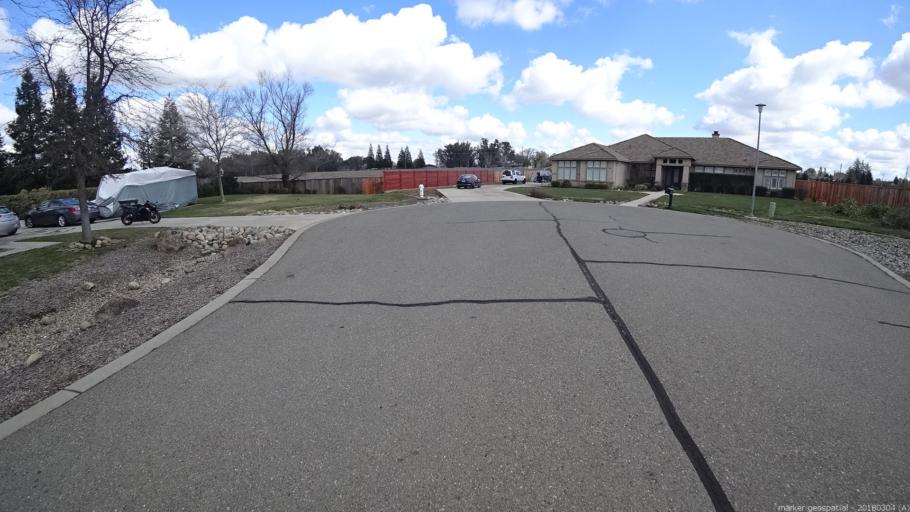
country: US
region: California
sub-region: Sacramento County
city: Vineyard
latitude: 38.4562
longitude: -121.3003
